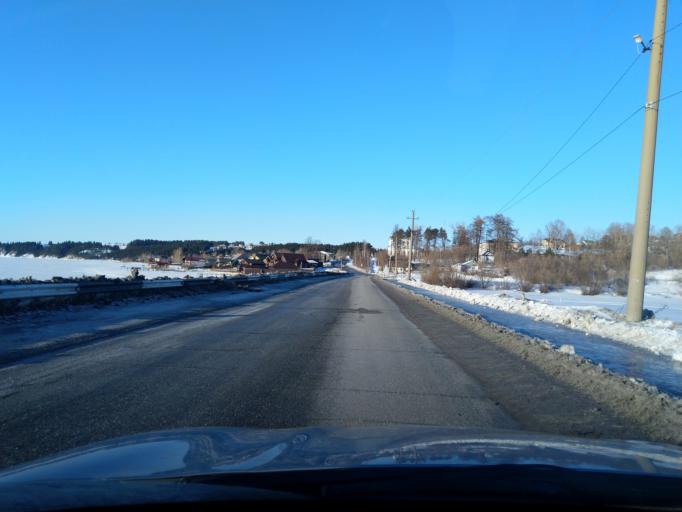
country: RU
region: Perm
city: Polazna
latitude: 58.3039
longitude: 56.4185
